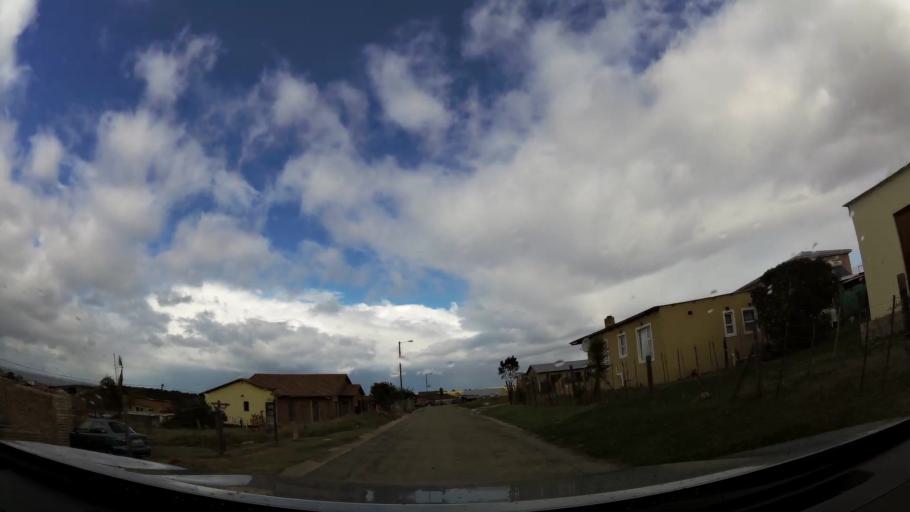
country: ZA
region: Western Cape
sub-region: Eden District Municipality
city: George
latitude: -34.0228
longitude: 22.4766
